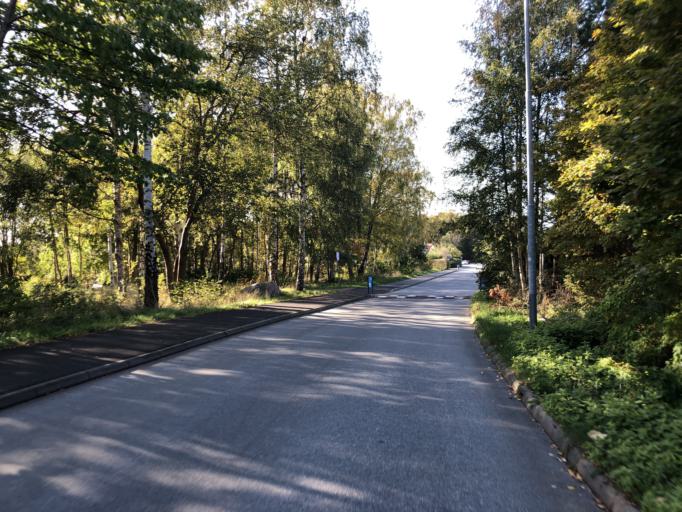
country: SE
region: Vaestra Goetaland
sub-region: Goteborg
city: Billdal
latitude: 57.6196
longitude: 11.8895
